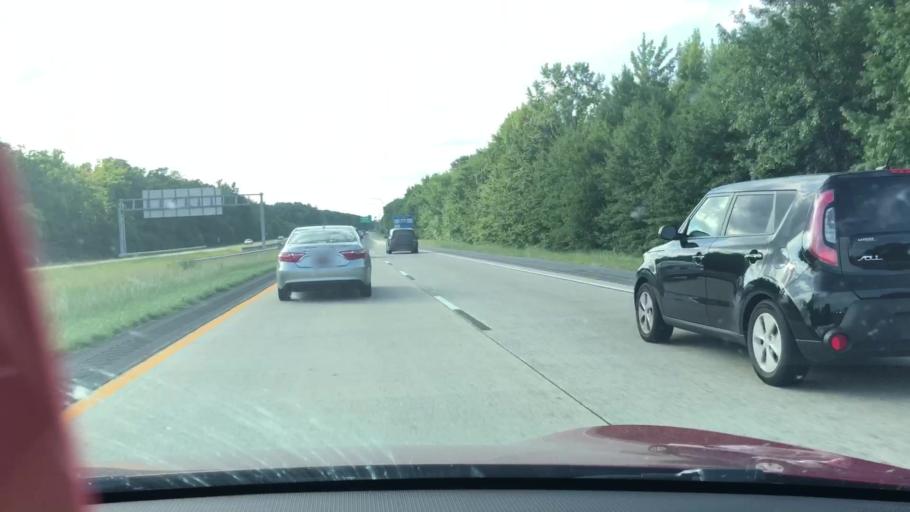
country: US
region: Delaware
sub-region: Kent County
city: Dover
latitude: 39.1969
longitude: -75.5322
